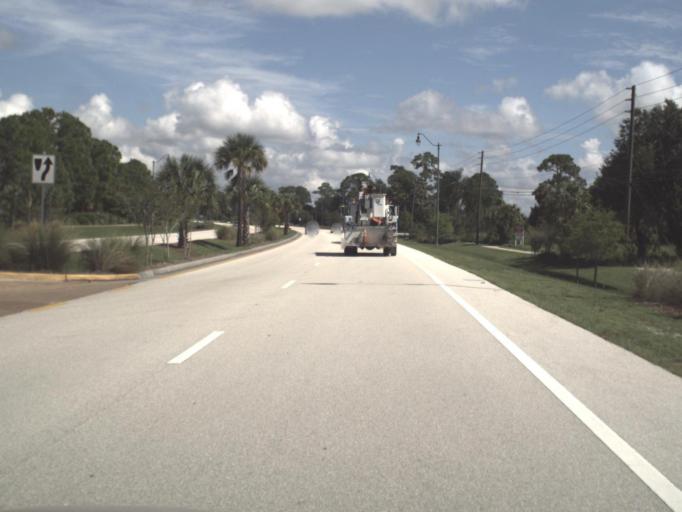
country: US
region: Florida
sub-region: Sarasota County
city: North Port
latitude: 27.0450
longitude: -82.1595
